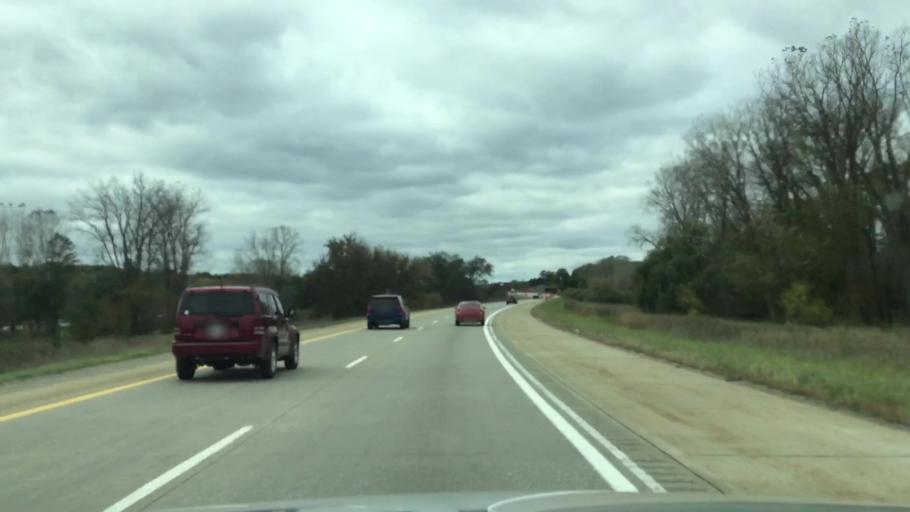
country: US
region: Michigan
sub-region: Jackson County
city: Michigan Center
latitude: 42.2817
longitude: -84.2933
